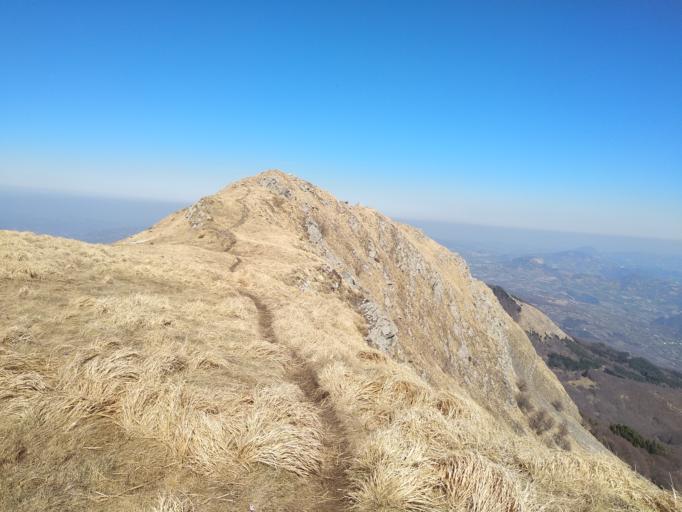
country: IT
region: Emilia-Romagna
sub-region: Provincia di Reggio Emilia
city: Collagna
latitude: 44.3776
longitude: 10.2895
